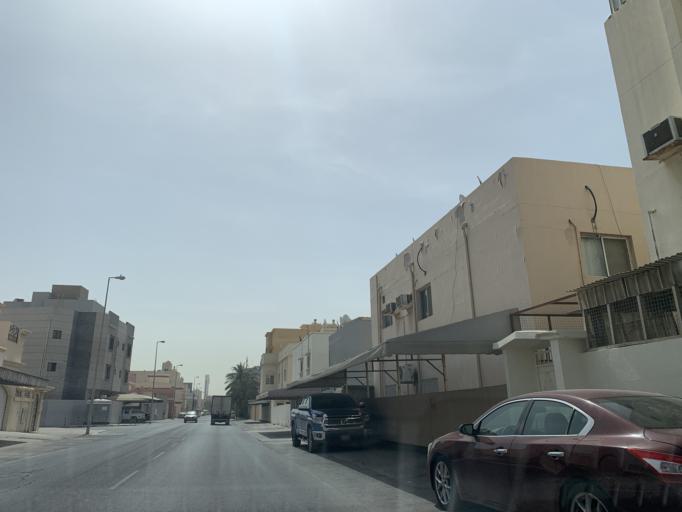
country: BH
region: Northern
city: Madinat `Isa
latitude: 26.1739
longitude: 50.5617
